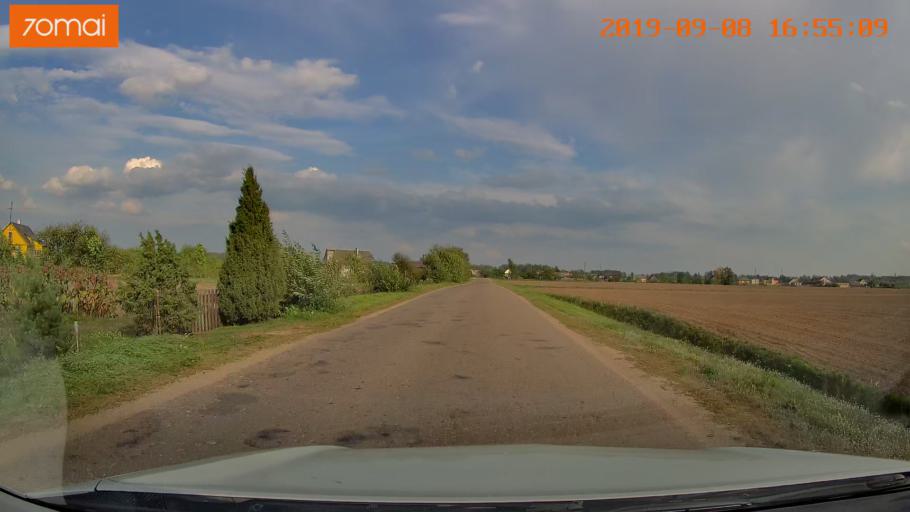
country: BY
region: Grodnenskaya
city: Hrodna
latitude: 53.7488
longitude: 23.9287
